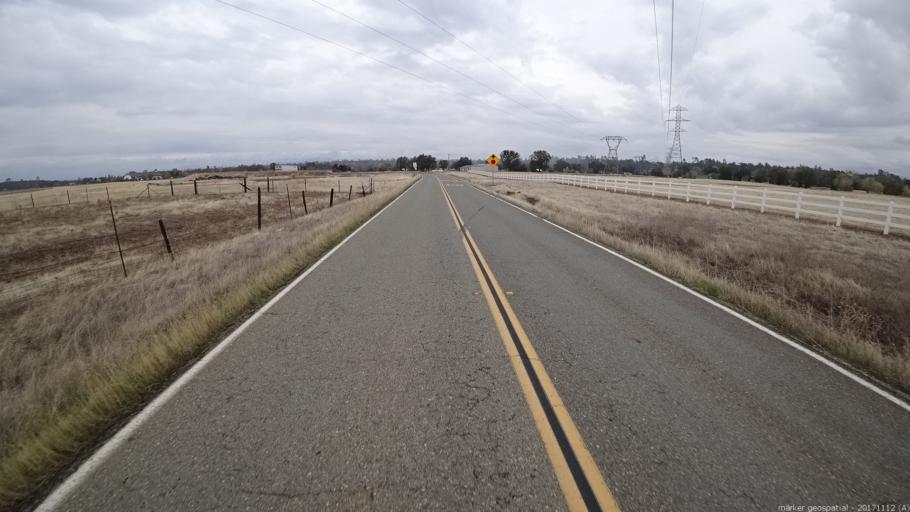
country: US
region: California
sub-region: Shasta County
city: Palo Cedro
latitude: 40.5367
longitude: -122.1740
